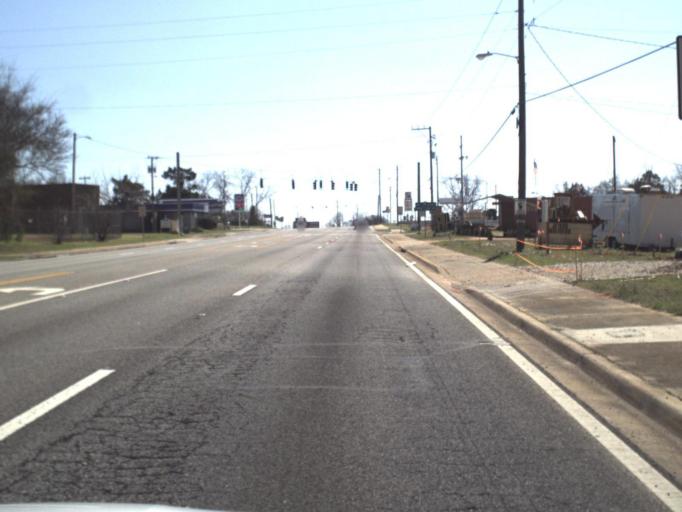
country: US
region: Florida
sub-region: Jackson County
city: Graceville
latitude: 30.9515
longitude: -85.4025
